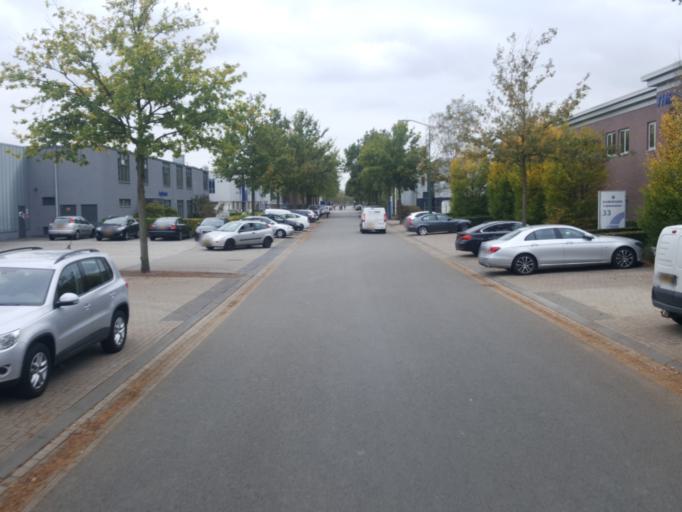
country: NL
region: North Brabant
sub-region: Gemeente Nuenen, Gerwen en Nederwetten
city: Nuenen
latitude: 51.4471
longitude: 5.5591
